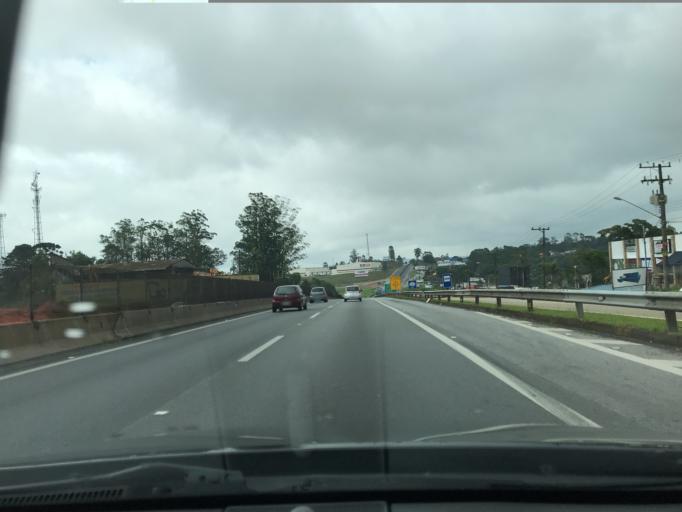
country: BR
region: Sao Paulo
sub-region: Cotia
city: Cotia
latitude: -23.6151
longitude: -46.9713
